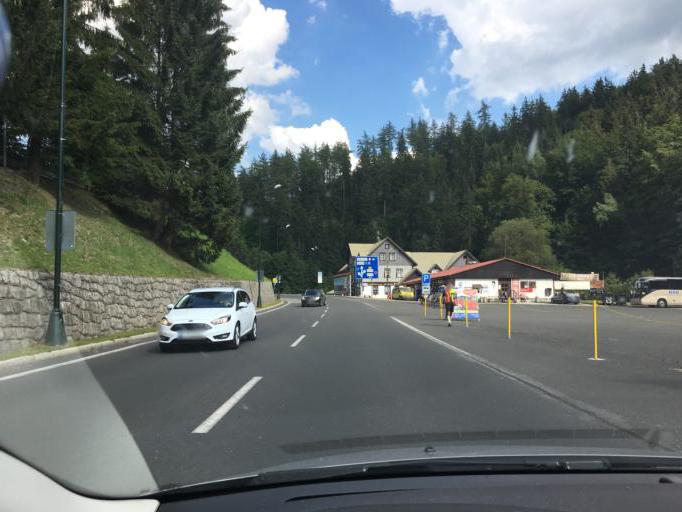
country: CZ
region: Kralovehradecky
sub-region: Okres Trutnov
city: Spindleruv Mlyn
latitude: 50.7245
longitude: 15.6029
